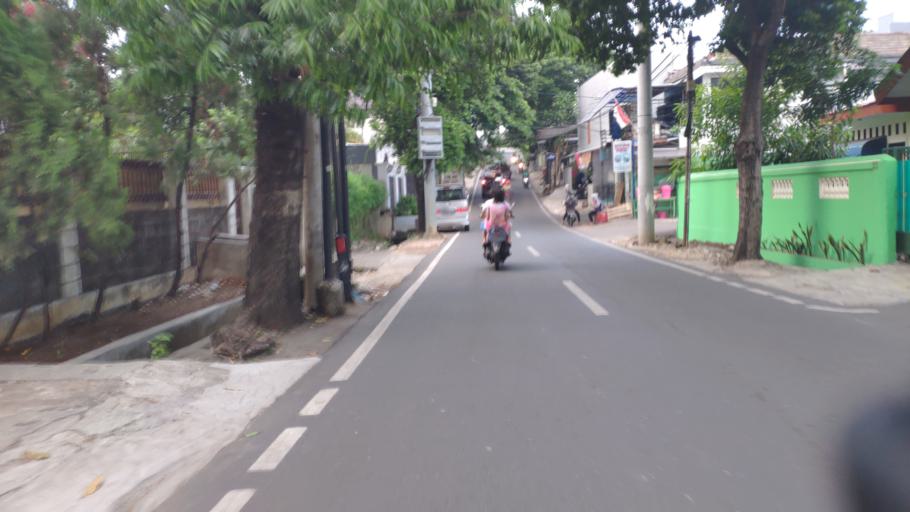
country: ID
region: West Java
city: Pamulang
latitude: -6.3061
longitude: 106.7986
